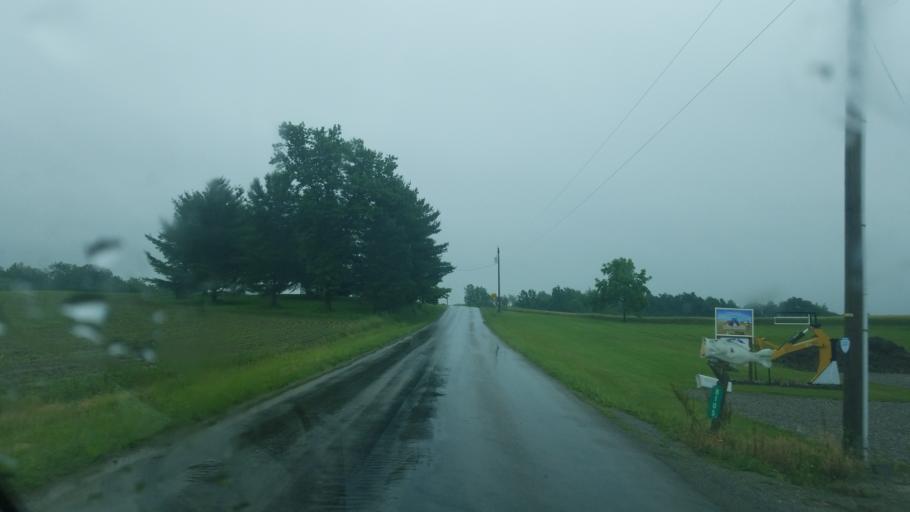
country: US
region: Ohio
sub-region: Huron County
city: Plymouth
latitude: 40.9827
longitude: -82.5934
